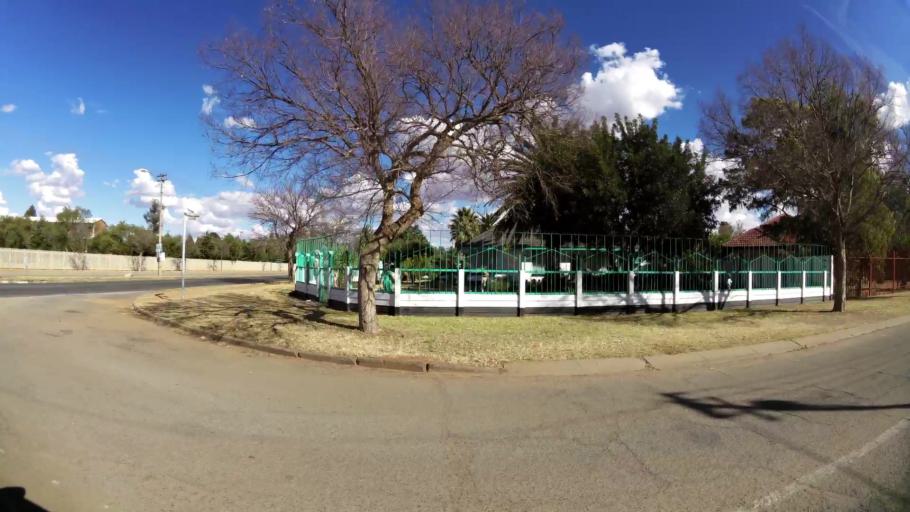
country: ZA
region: North-West
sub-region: Dr Kenneth Kaunda District Municipality
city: Klerksdorp
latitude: -26.8597
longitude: 26.6428
